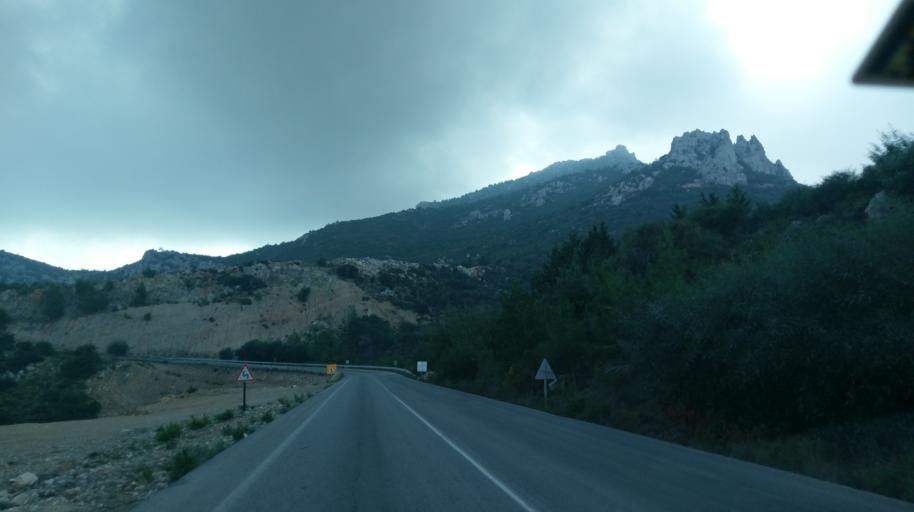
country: CY
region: Keryneia
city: Kyrenia
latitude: 35.2932
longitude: 33.4428
